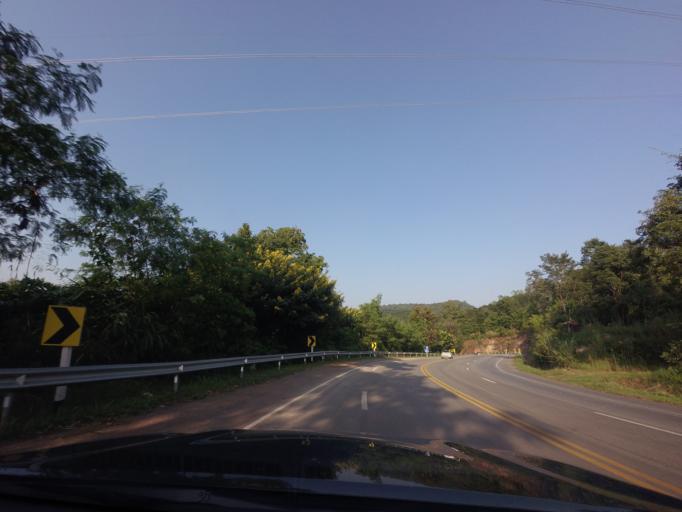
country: TH
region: Loei
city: Dan Sai
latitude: 17.2267
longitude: 101.1503
